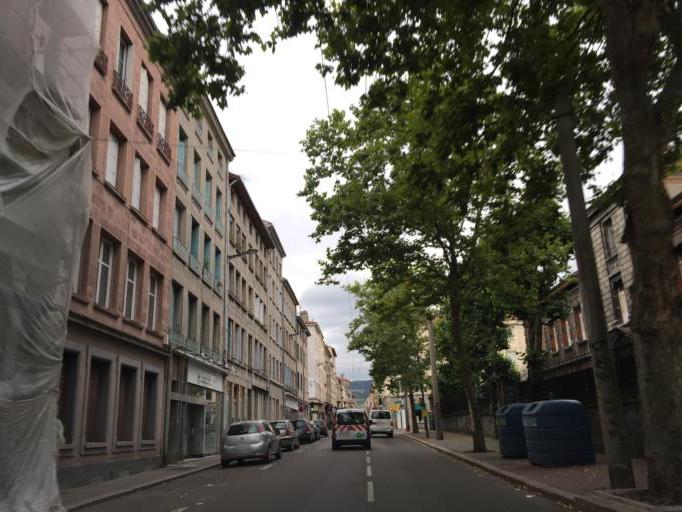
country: FR
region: Rhone-Alpes
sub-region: Departement de la Loire
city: Saint-Etienne
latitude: 45.4330
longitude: 4.3924
